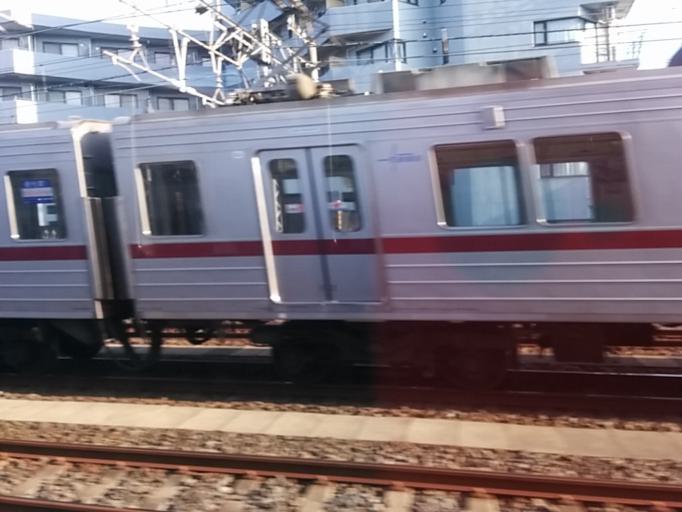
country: JP
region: Saitama
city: Shiki
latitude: 35.8241
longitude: 139.5723
